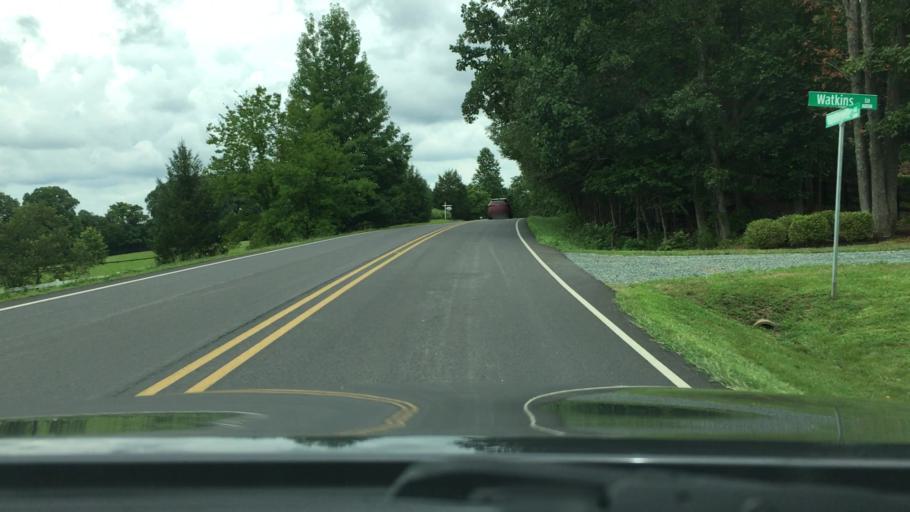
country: US
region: Virginia
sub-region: Orange County
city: Gordonsville
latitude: 38.1159
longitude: -78.2397
